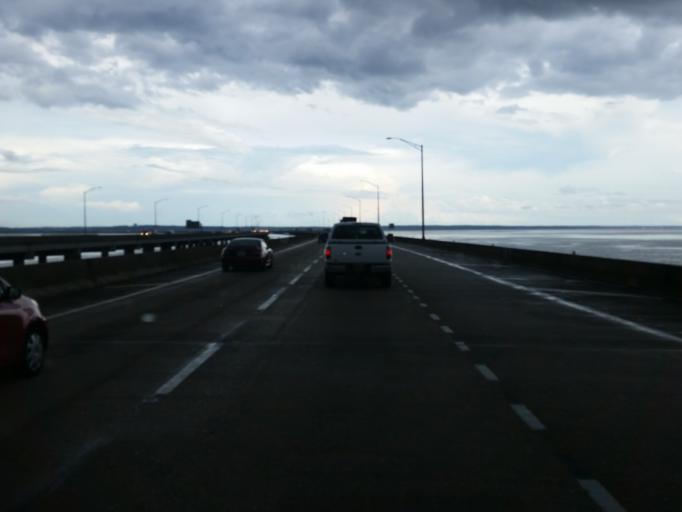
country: US
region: Alabama
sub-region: Mobile County
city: Mobile
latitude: 30.6752
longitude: -87.9838
